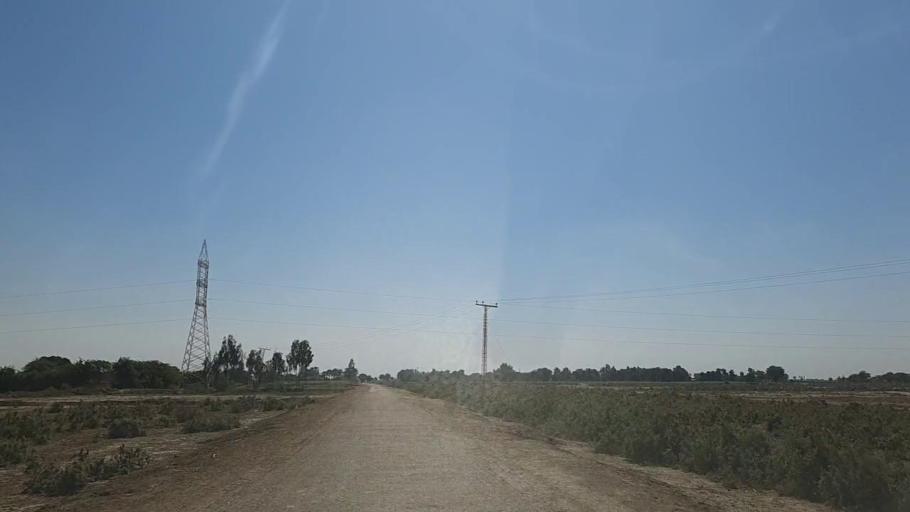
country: PK
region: Sindh
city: Samaro
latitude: 25.2968
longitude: 69.5029
